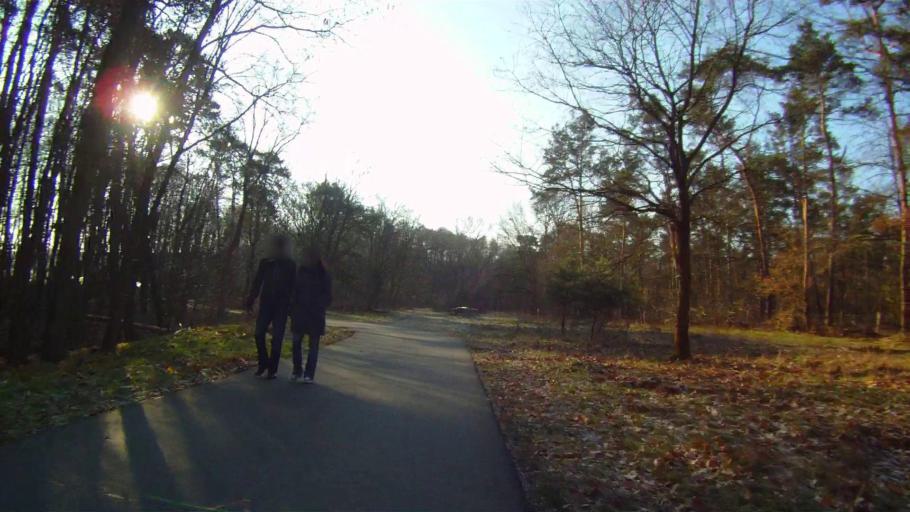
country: DE
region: Berlin
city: Friedrichshagen
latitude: 52.4328
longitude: 13.6196
